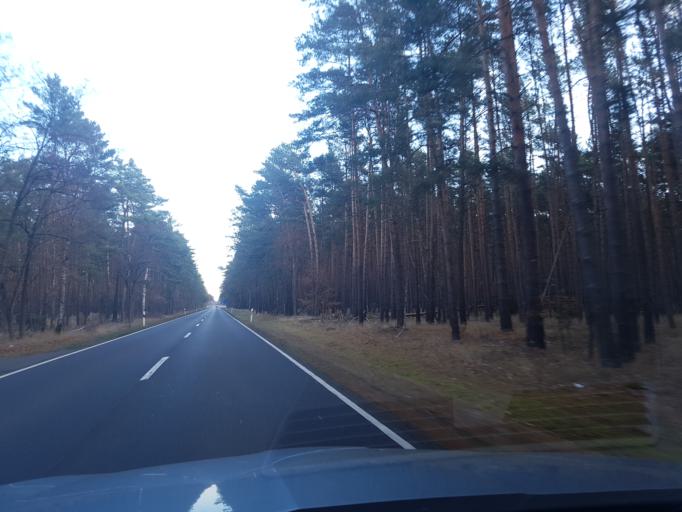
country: DE
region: Brandenburg
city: Kasel-Golzig
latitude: 52.0113
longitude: 13.6866
